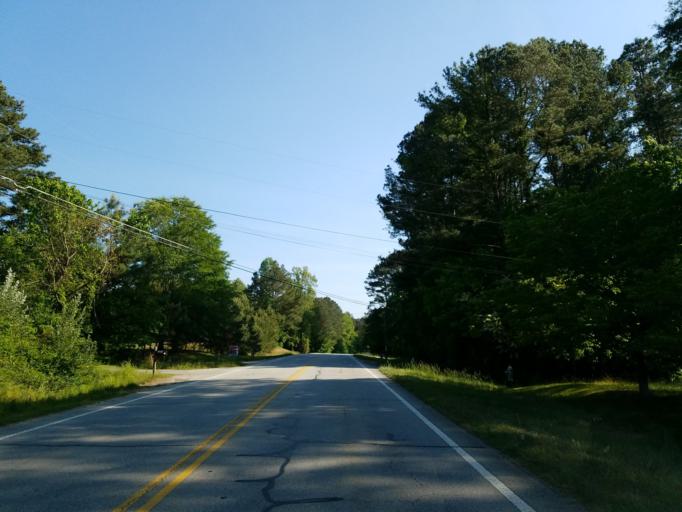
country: US
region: Georgia
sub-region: Paulding County
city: Dallas
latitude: 33.8788
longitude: -84.8840
